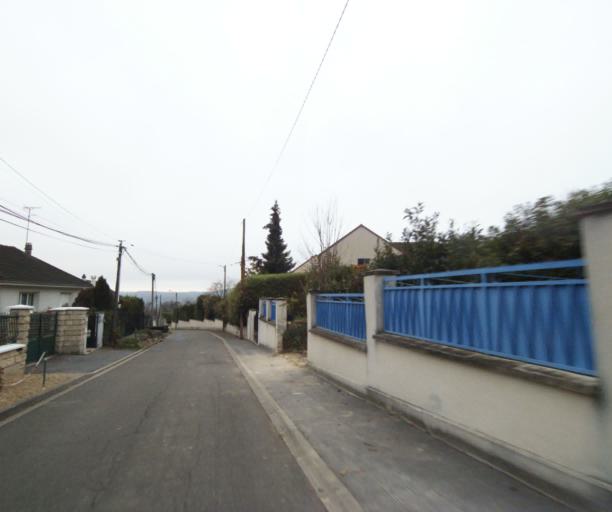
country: FR
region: Ile-de-France
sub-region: Departement des Yvelines
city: Triel-sur-Seine
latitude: 48.9871
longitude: 2.0048
